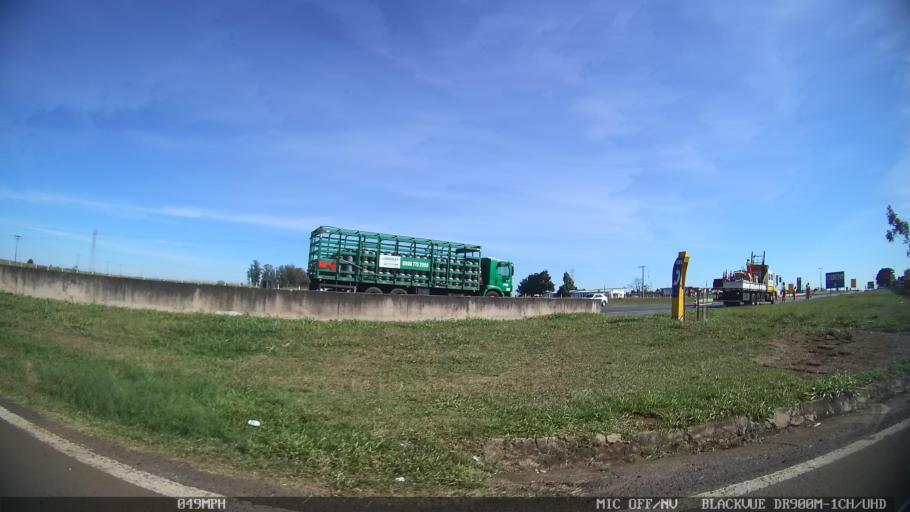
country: BR
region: Sao Paulo
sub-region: Pirassununga
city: Pirassununga
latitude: -22.0813
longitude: -47.4213
